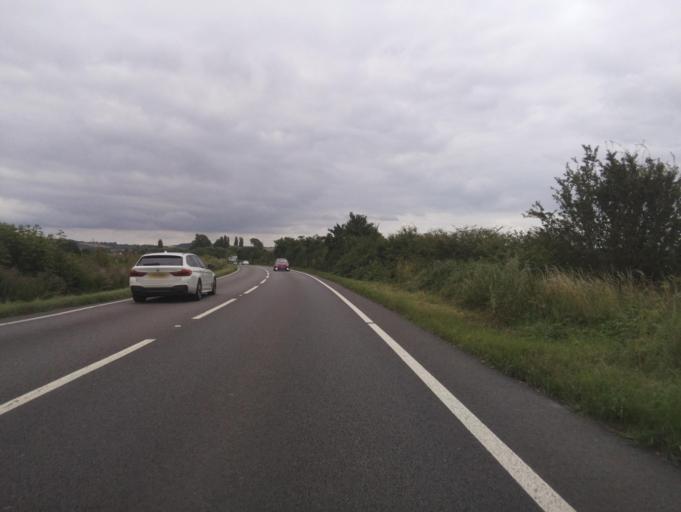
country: GB
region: England
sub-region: Lincolnshire
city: Barrowby
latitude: 52.9313
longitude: -0.7392
